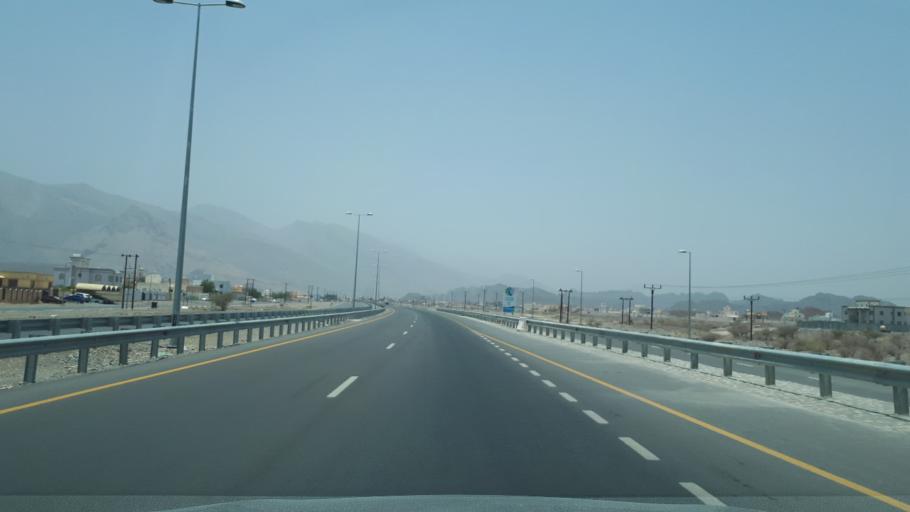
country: OM
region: Al Batinah
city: Rustaq
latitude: 23.4166
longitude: 57.3624
